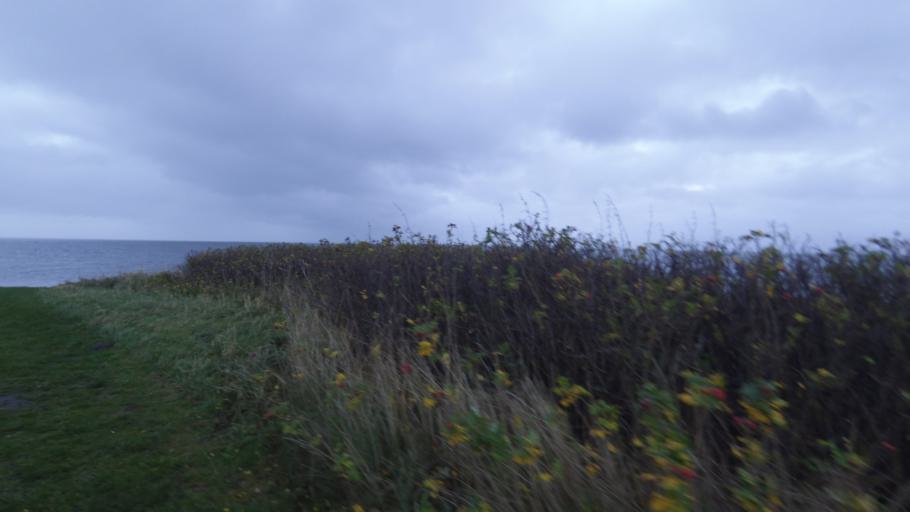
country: DK
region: Central Jutland
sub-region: Arhus Kommune
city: Beder
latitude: 56.0203
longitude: 10.2810
